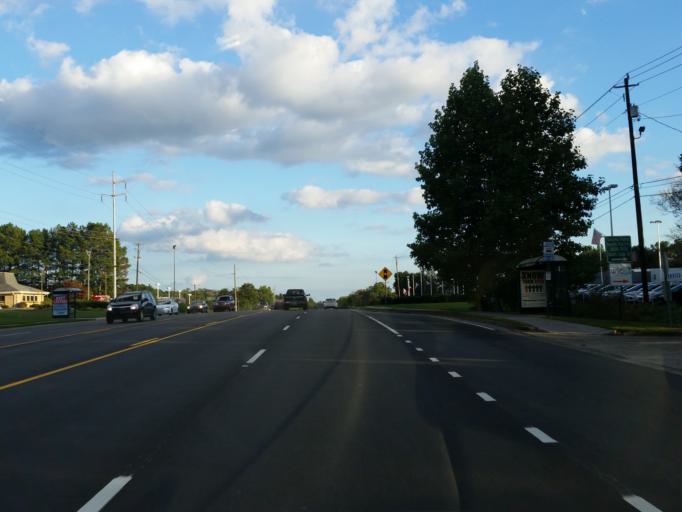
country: US
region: Georgia
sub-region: Cobb County
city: Smyrna
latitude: 33.8613
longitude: -84.5190
